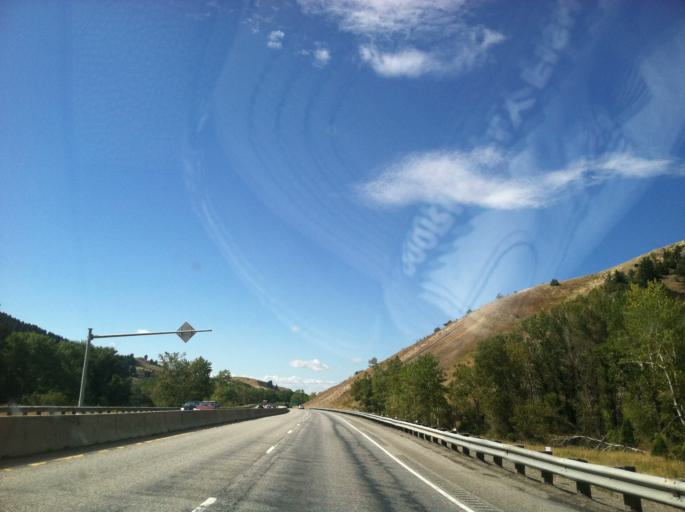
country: US
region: Montana
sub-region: Gallatin County
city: Bozeman
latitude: 45.6418
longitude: -110.9212
